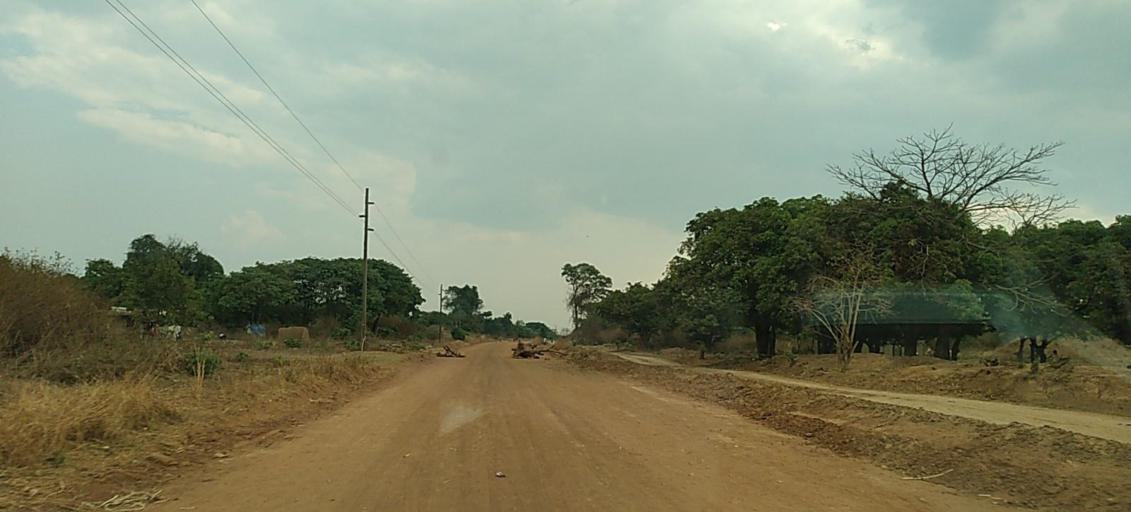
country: ZM
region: Copperbelt
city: Kalulushi
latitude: -12.8966
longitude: 27.9497
